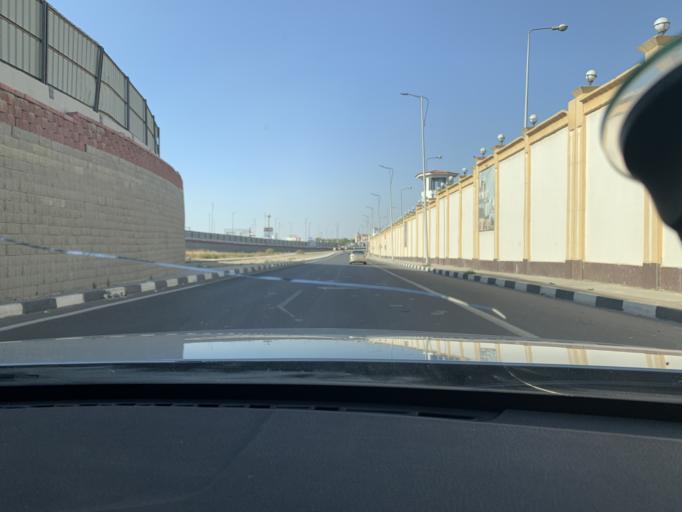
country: EG
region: Muhafazat al Qahirah
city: Cairo
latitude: 30.0510
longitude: 31.4109
